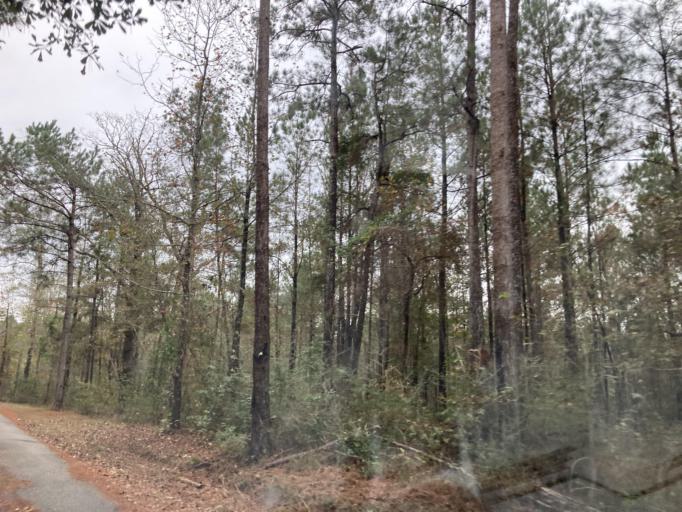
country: US
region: Mississippi
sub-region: Lamar County
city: Purvis
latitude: 31.1945
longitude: -89.4474
